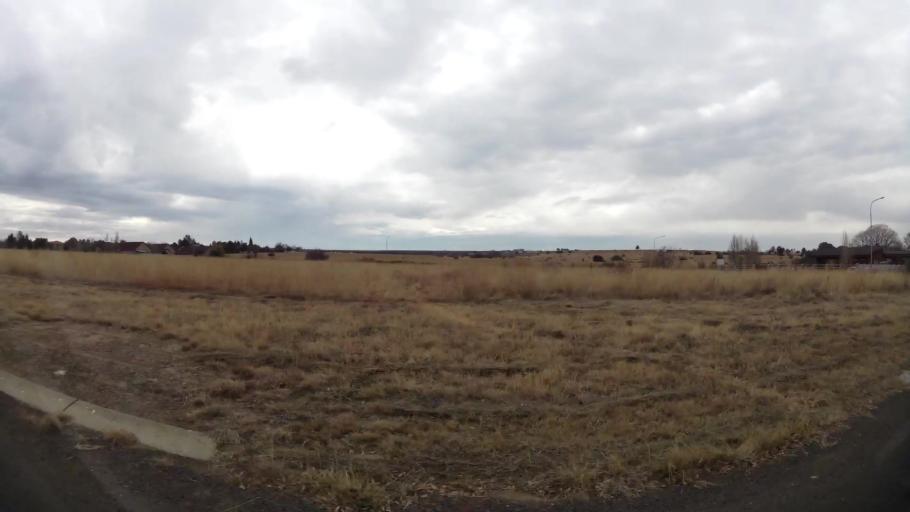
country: ZA
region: Orange Free State
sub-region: Fezile Dabi District Municipality
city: Kroonstad
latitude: -27.6311
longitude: 27.2451
